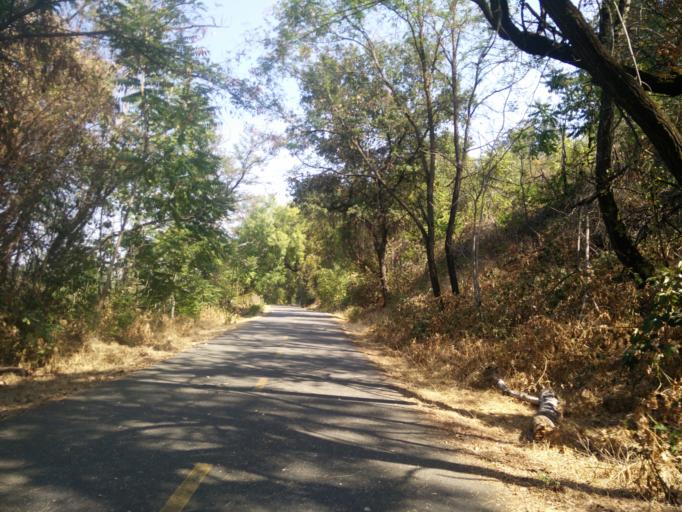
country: US
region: California
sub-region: Shasta County
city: Redding
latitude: 40.5921
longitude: -122.4139
